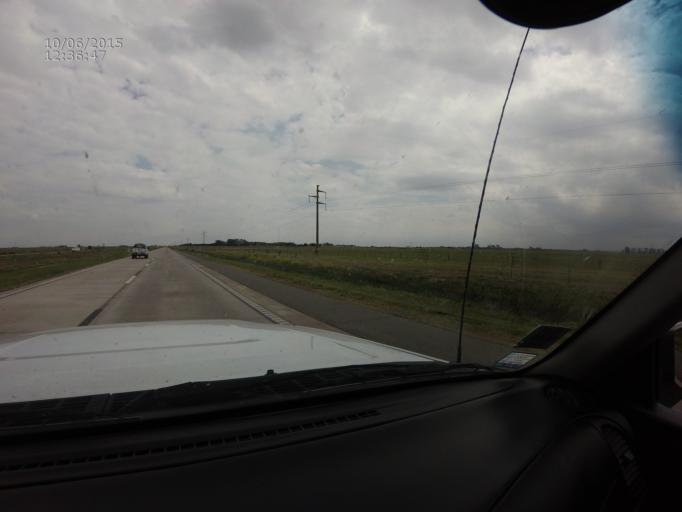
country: AR
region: Santa Fe
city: Carcarana
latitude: -32.8701
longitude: -61.2056
